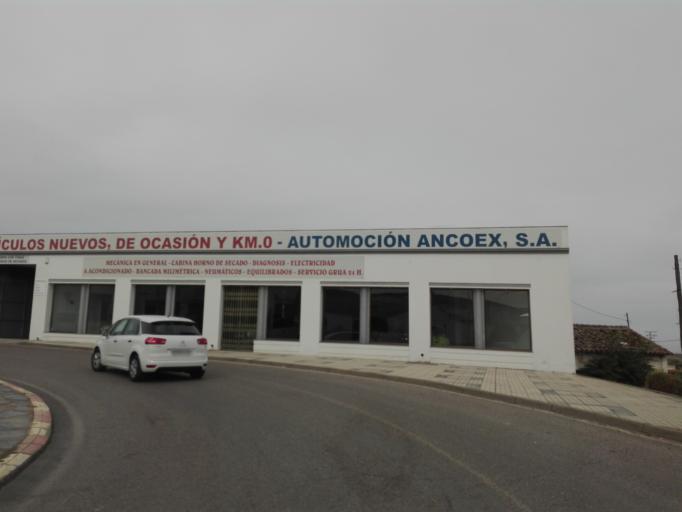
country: ES
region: Extremadura
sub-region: Provincia de Badajoz
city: Llerena
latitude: 38.2412
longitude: -6.0154
